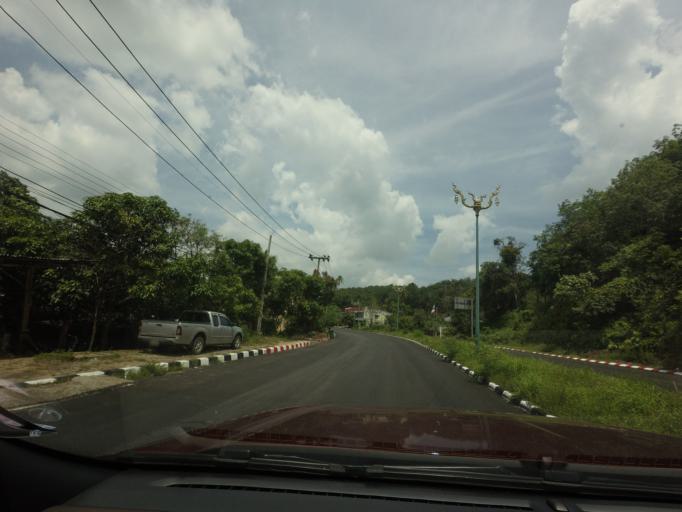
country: TH
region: Yala
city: Betong
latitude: 5.7674
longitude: 101.0515
